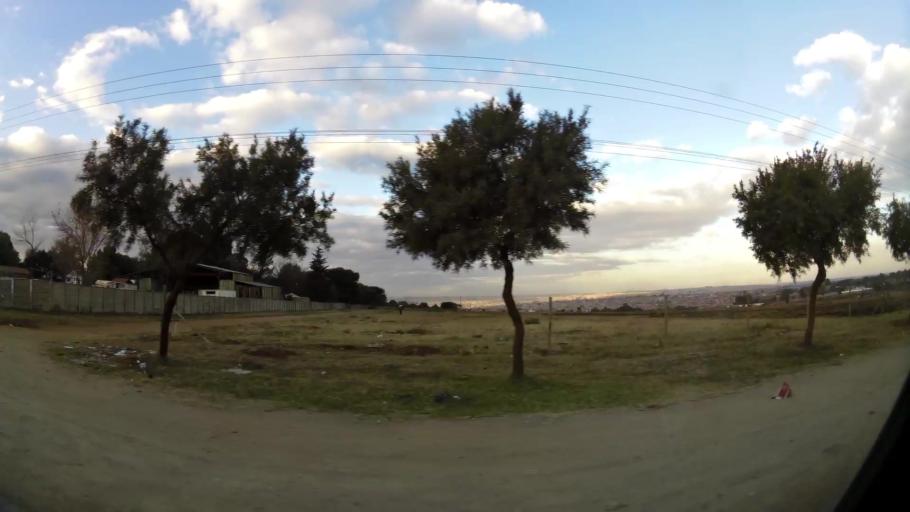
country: ZA
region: Gauteng
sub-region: City of Johannesburg Metropolitan Municipality
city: Midrand
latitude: -25.9942
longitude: 28.1547
